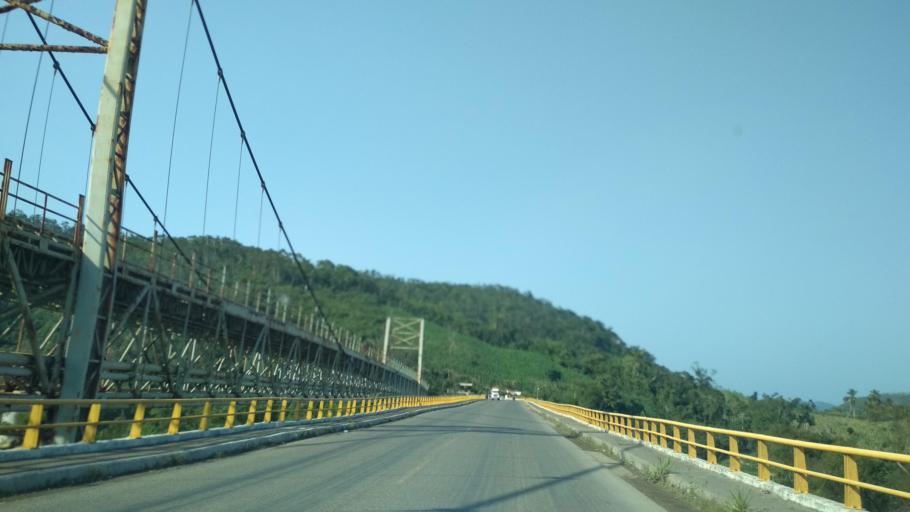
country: MX
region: Veracruz
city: Agua Dulce
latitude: 20.3963
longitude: -97.2389
